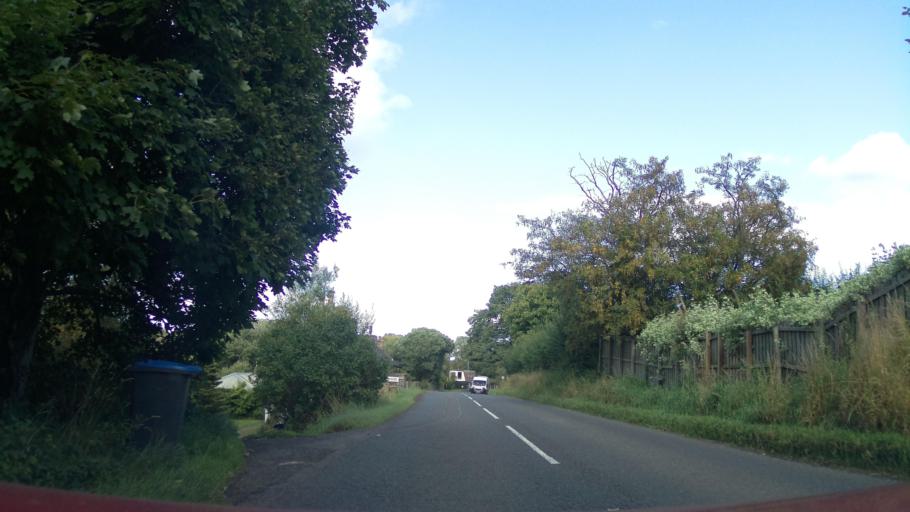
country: GB
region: Scotland
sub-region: The Scottish Borders
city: West Linton
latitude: 55.7244
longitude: -3.3283
